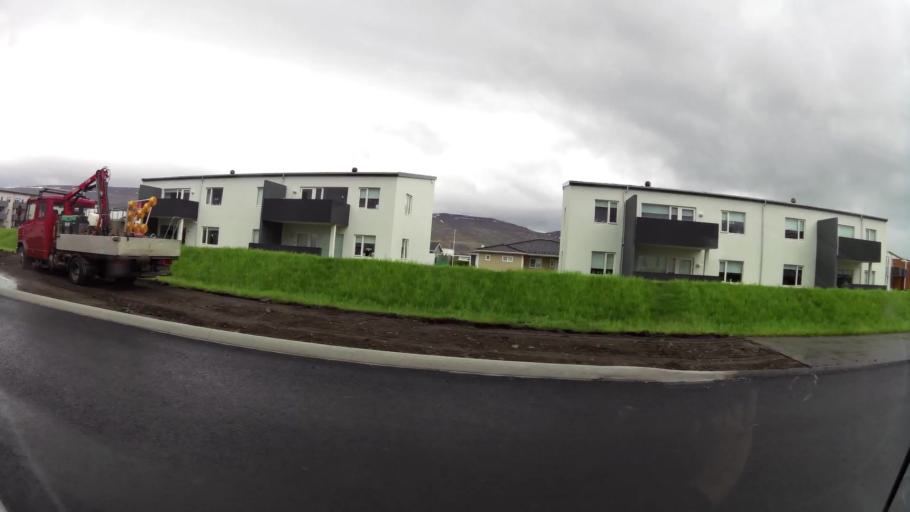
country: IS
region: Northeast
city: Akureyri
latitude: 65.6677
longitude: -18.1079
